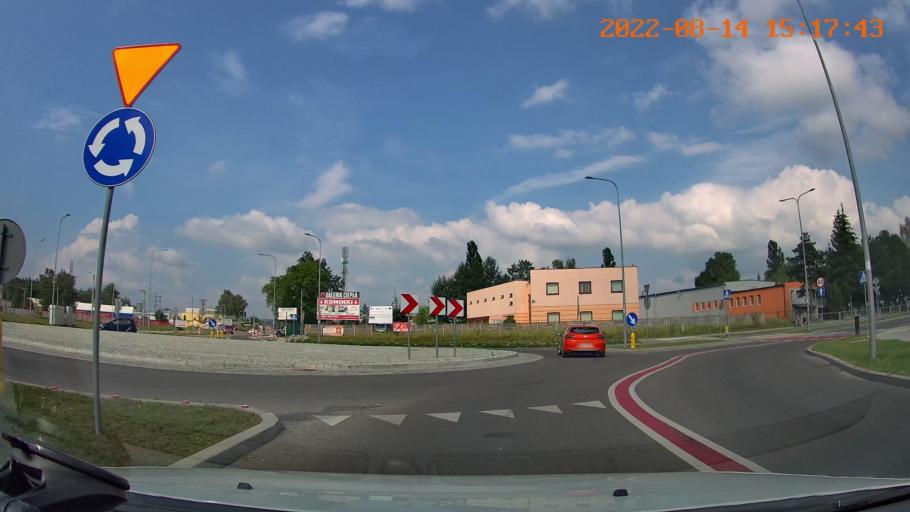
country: PL
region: Swietokrzyskie
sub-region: Powiat kielecki
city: Kielce
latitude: 50.9000
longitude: 20.6338
